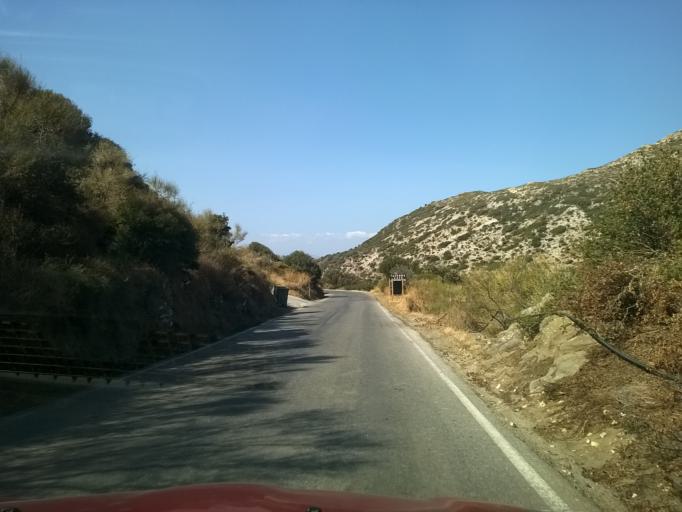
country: GR
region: South Aegean
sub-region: Nomos Kykladon
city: Filotion
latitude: 37.0777
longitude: 25.4927
